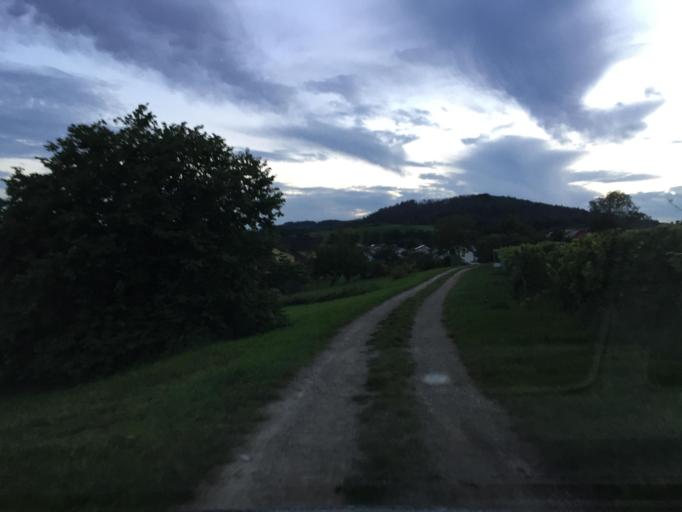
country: CH
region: Schaffhausen
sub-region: Bezirk Unterklettgau
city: Wilchingen
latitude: 47.6649
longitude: 8.4259
